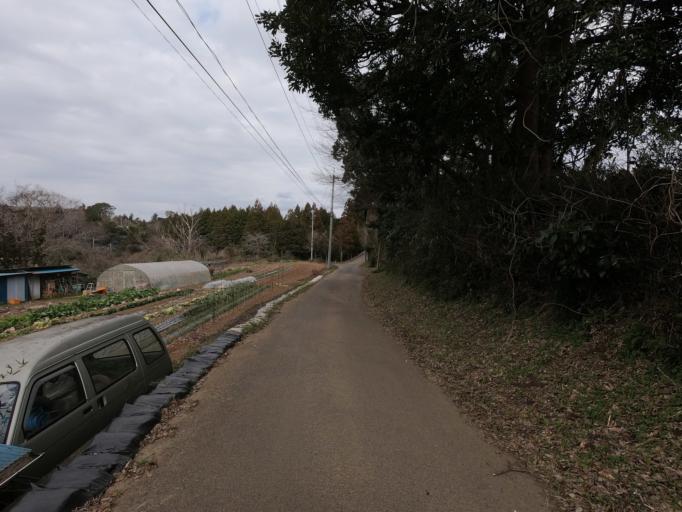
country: JP
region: Ibaraki
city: Itako
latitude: 36.0587
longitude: 140.4497
